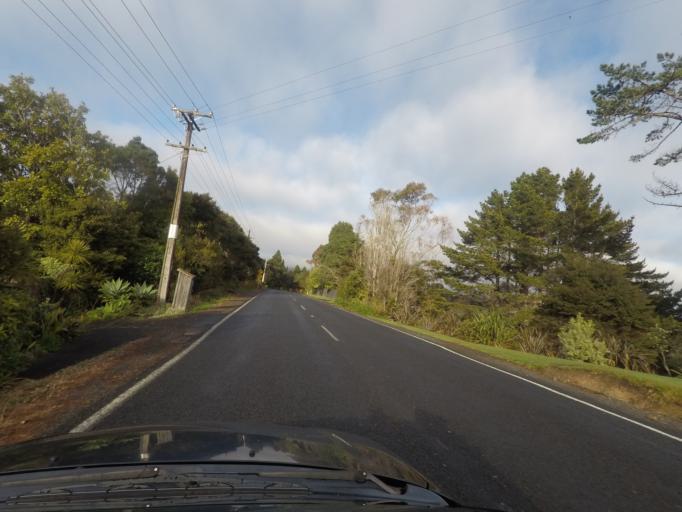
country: NZ
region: Auckland
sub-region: Auckland
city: Waitakere
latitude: -36.9124
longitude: 174.6061
